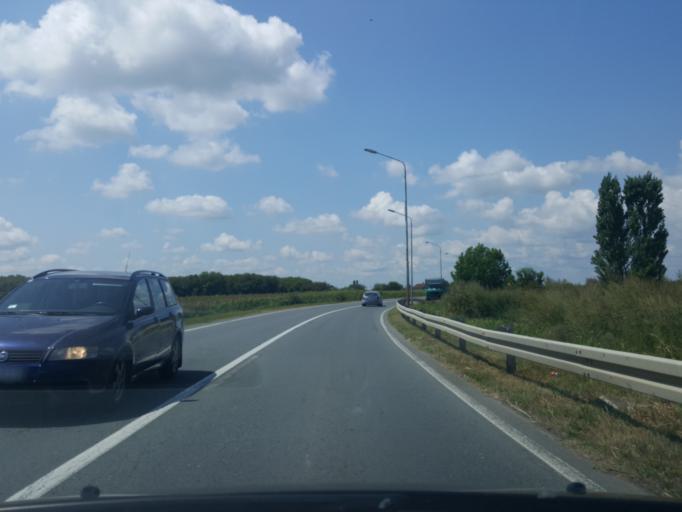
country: RS
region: Autonomna Pokrajina Vojvodina
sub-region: Sremski Okrug
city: Sremska Mitrovica
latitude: 44.9518
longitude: 19.6290
